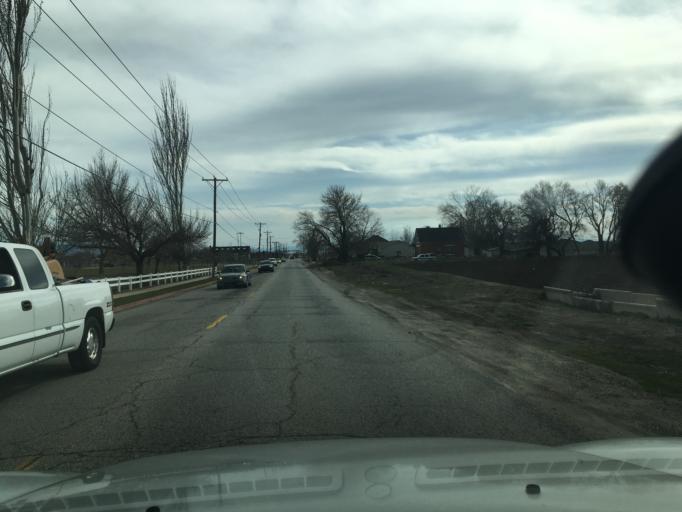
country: US
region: Utah
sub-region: Davis County
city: Layton
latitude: 41.0720
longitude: -112.0070
